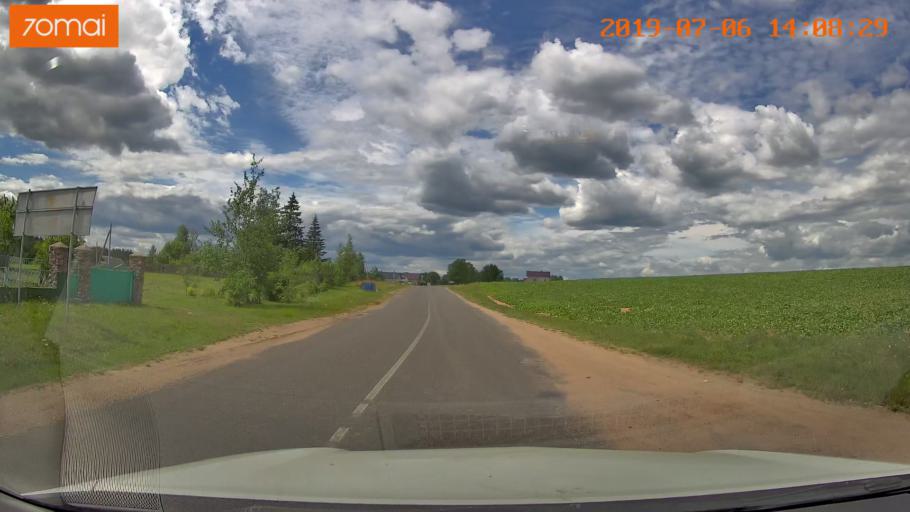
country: BY
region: Minsk
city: Ivyanyets
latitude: 53.8755
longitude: 26.7578
